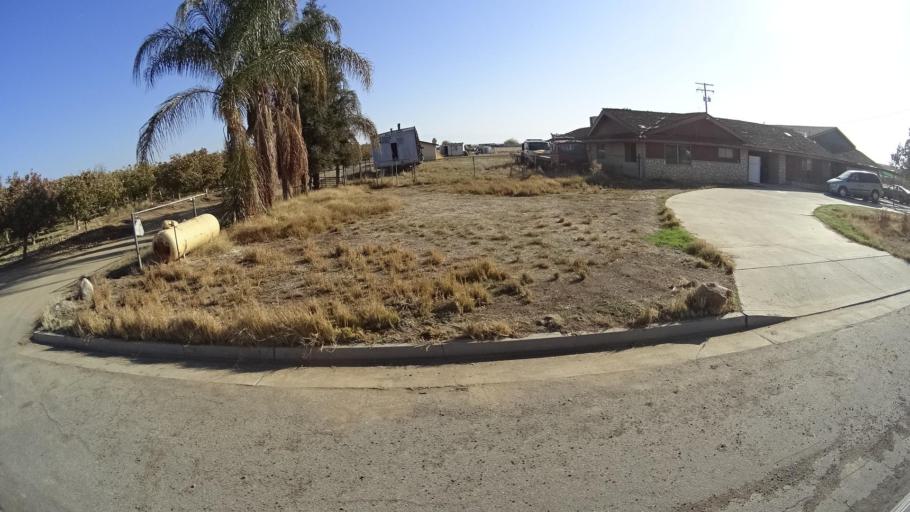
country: US
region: California
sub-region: Tulare County
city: Richgrove
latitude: 35.7541
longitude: -119.1341
